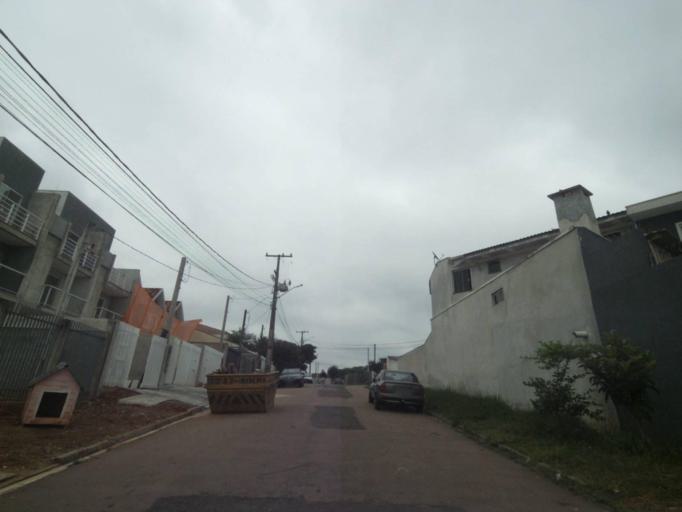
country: BR
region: Parana
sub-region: Curitiba
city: Curitiba
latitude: -25.4887
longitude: -49.3536
